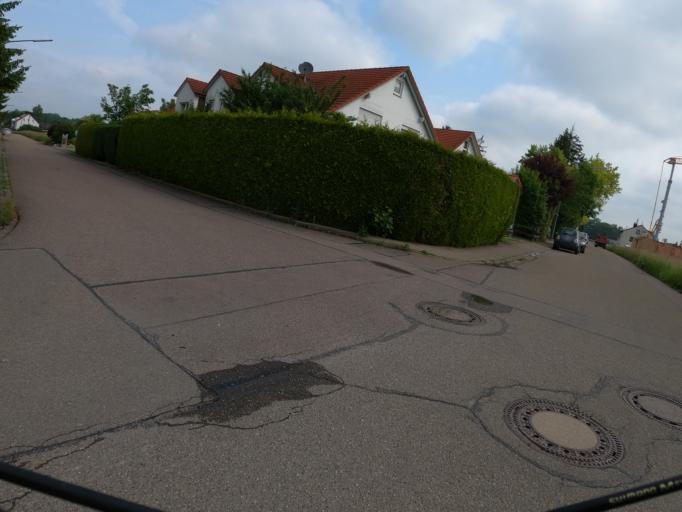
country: DE
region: Bavaria
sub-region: Swabia
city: Nersingen
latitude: 48.4301
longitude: 10.1138
